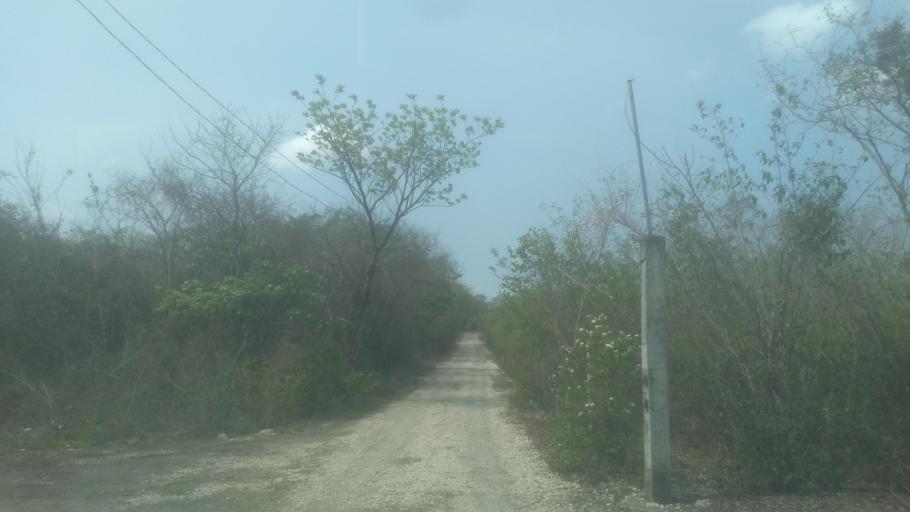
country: MX
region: Veracruz
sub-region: Emiliano Zapata
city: Plan del Rio
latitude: 19.3897
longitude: -96.6288
